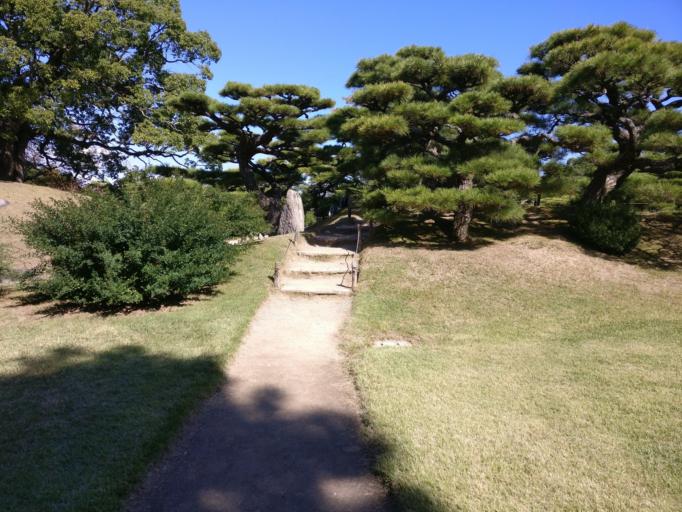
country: JP
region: Kagawa
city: Takamatsu-shi
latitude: 34.3283
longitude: 134.0439
